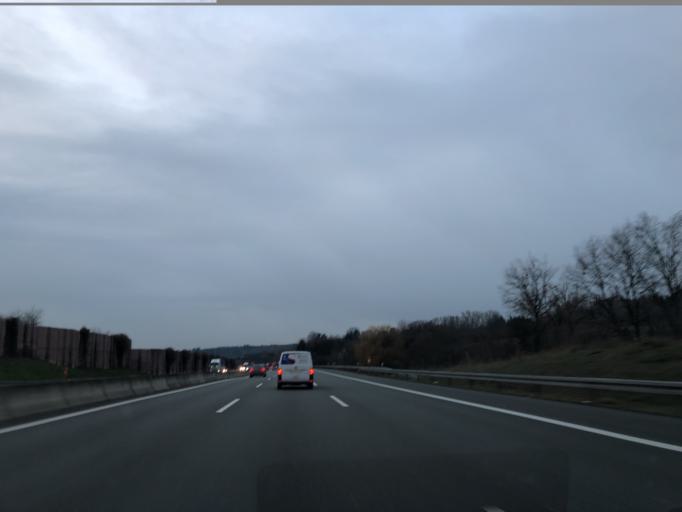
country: DE
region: Bavaria
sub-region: Regierungsbezirk Unterfranken
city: Glattbach
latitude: 49.9932
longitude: 9.1458
